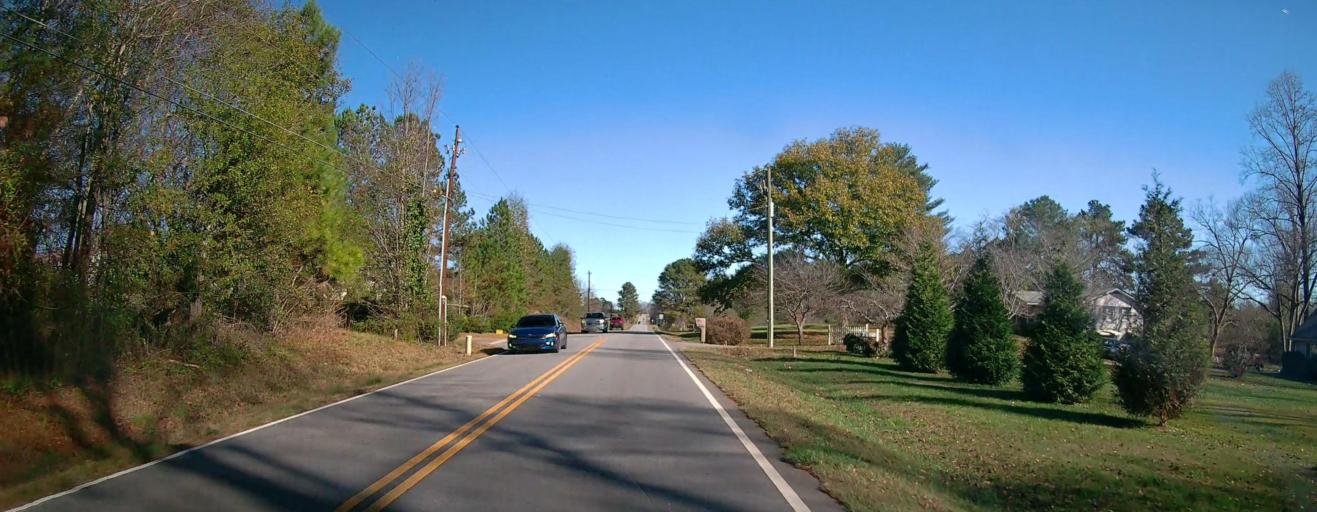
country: US
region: Georgia
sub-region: White County
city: Cleveland
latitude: 34.4775
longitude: -83.7647
